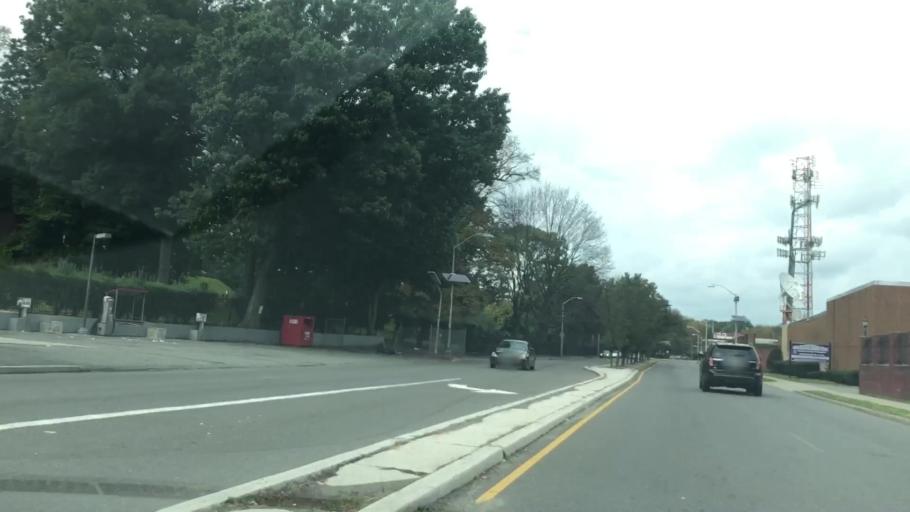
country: US
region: New Jersey
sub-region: Essex County
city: Orange
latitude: 40.7827
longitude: -74.2207
